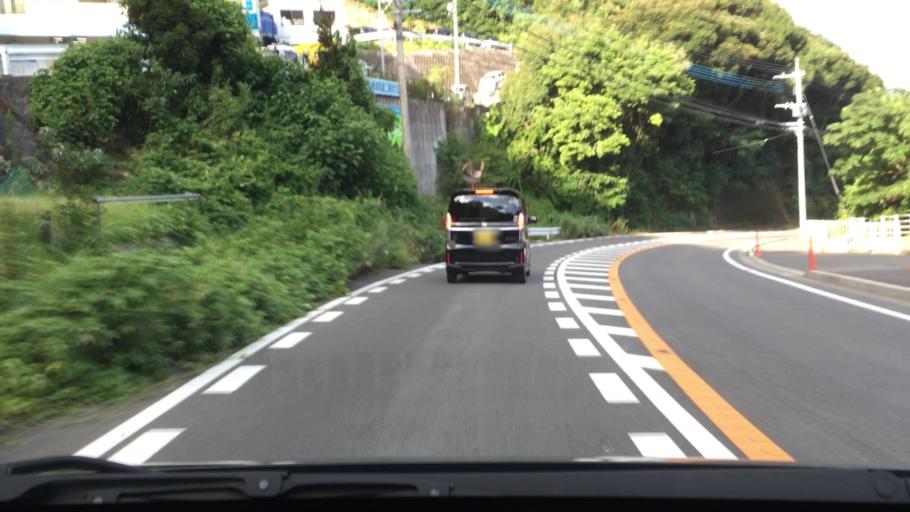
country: JP
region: Nagasaki
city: Togitsu
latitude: 32.8103
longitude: 129.8166
